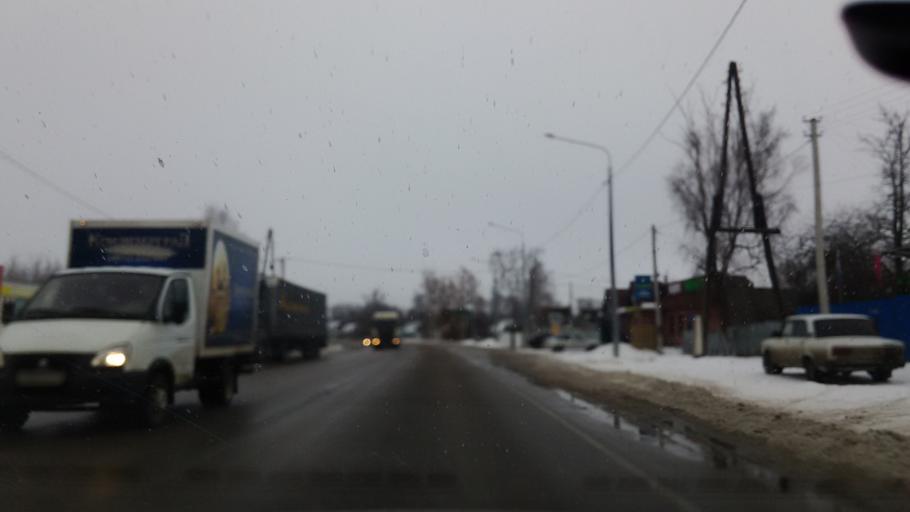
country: RU
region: Tula
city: Bolokhovo
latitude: 54.0500
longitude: 37.8228
